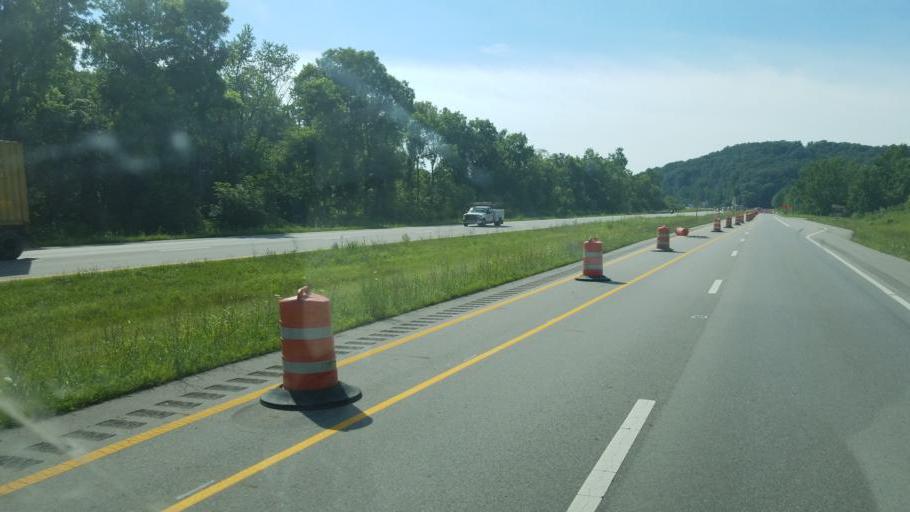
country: US
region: Ohio
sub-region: Athens County
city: Chauncey
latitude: 39.4010
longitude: -82.1655
